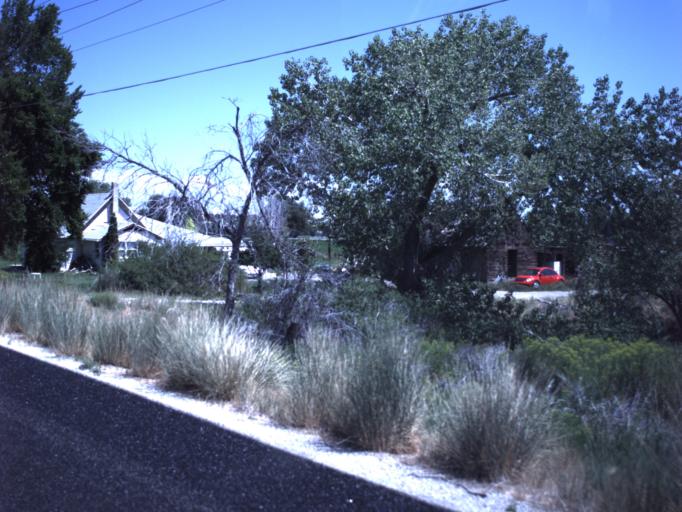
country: US
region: Utah
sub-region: Emery County
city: Ferron
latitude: 39.0732
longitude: -111.1316
